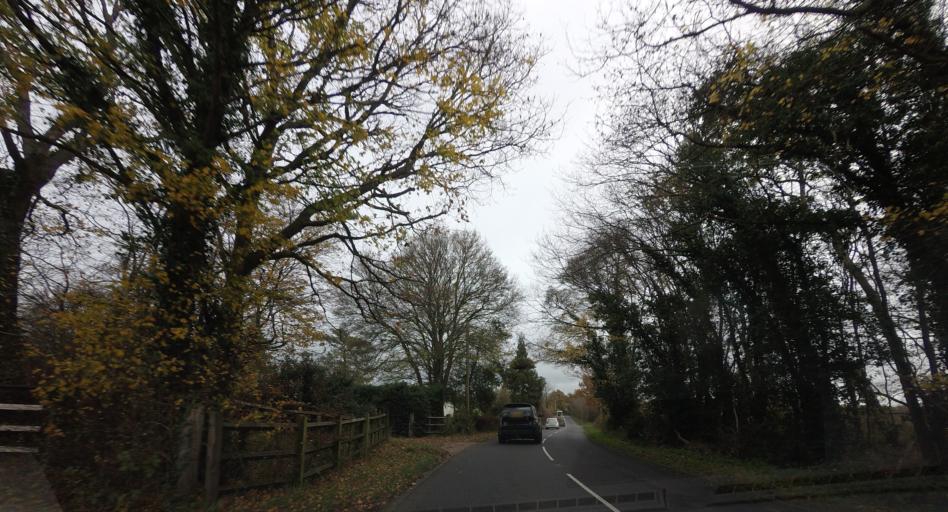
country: GB
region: England
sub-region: East Sussex
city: Northiam
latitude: 50.9988
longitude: 0.6324
